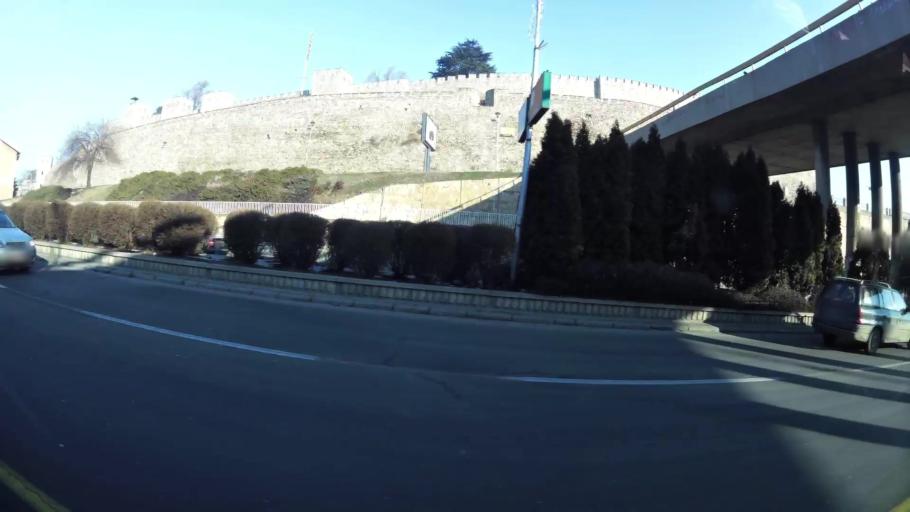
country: MK
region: Karpos
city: Skopje
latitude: 41.9983
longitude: 21.4333
